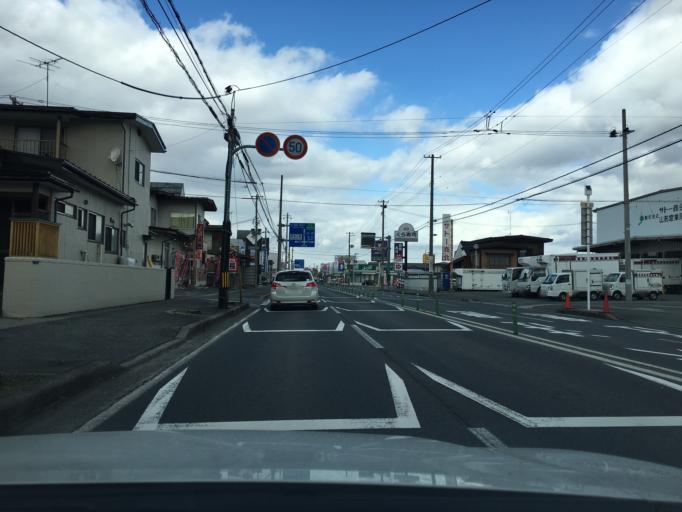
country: JP
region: Yamagata
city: Yamagata-shi
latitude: 38.2357
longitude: 140.3060
